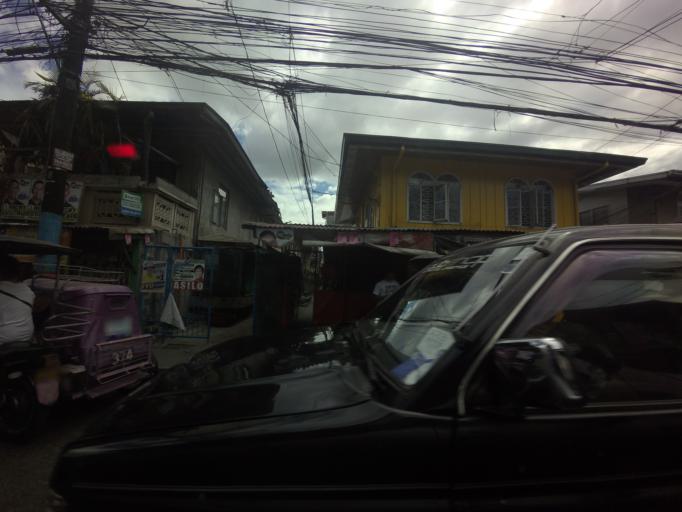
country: PH
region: Calabarzon
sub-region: Province of Rizal
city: Pateros
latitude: 14.5575
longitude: 121.0911
